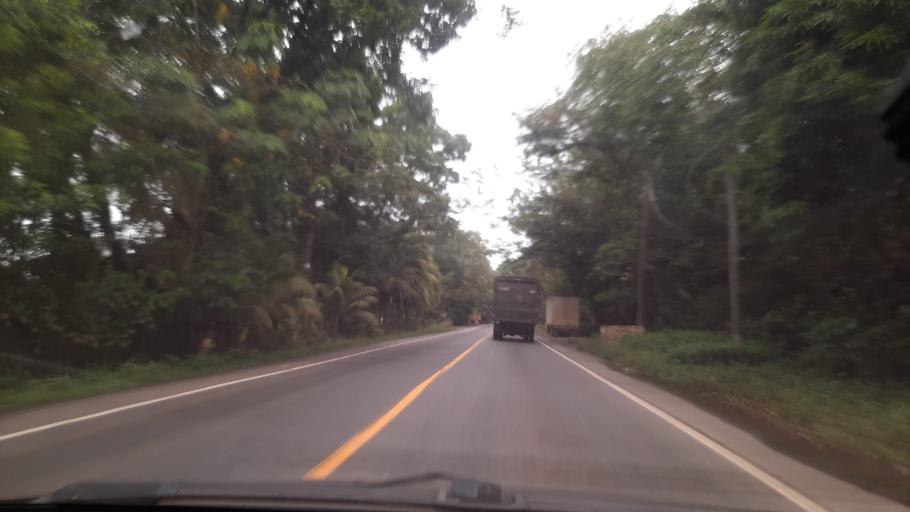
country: GT
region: Izabal
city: Morales
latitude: 15.4628
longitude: -88.9248
